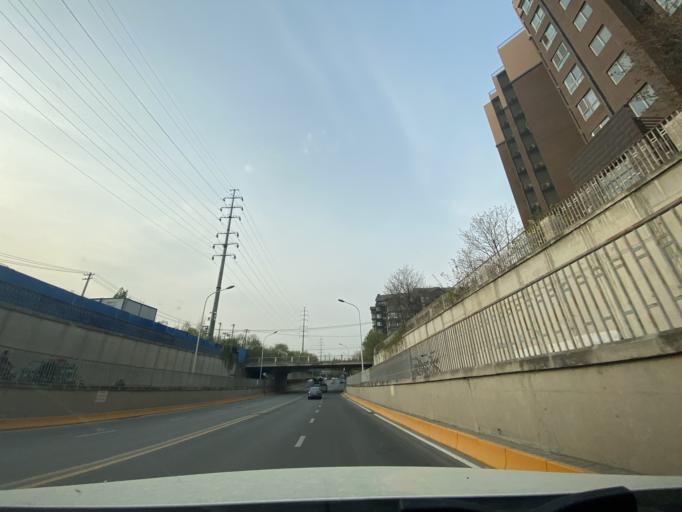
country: CN
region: Beijing
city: Babaoshan
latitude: 39.9303
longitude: 116.2328
